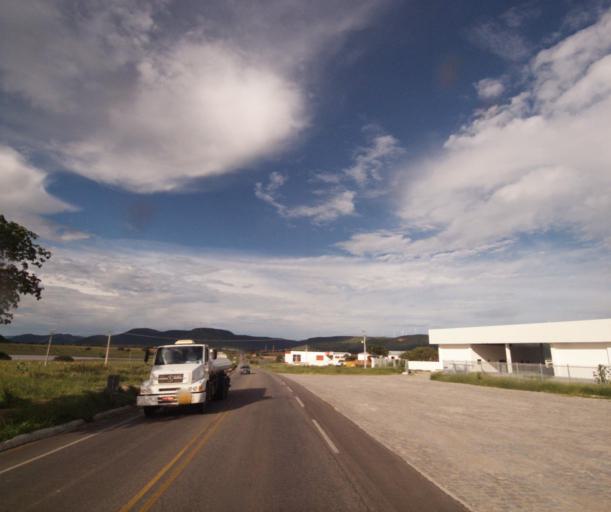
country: BR
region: Bahia
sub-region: Guanambi
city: Guanambi
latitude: -14.1899
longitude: -42.7426
